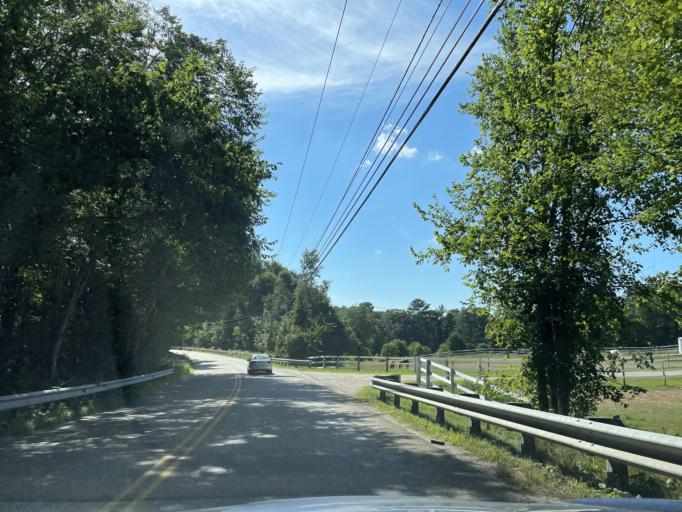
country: US
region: Massachusetts
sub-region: Worcester County
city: Oxford
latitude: 42.1220
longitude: -71.9053
